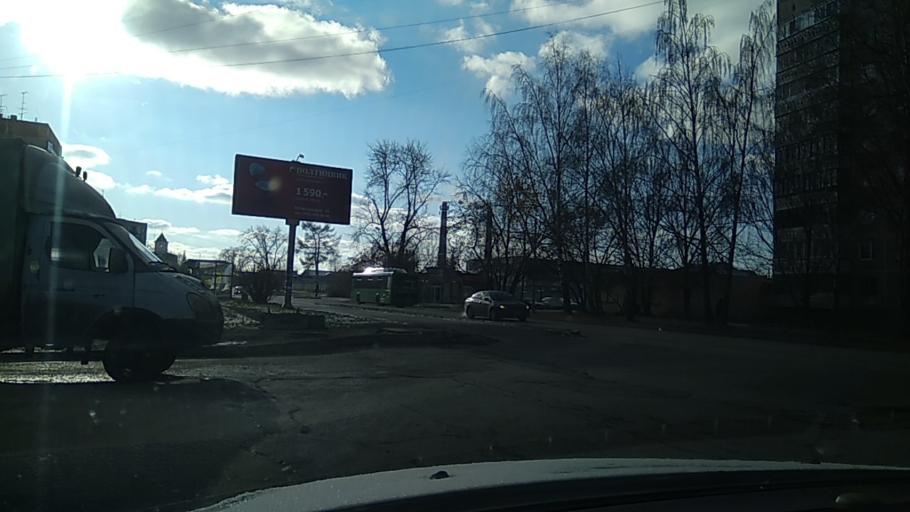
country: RU
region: Sverdlovsk
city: Sovkhoznyy
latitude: 56.7447
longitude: 60.6140
